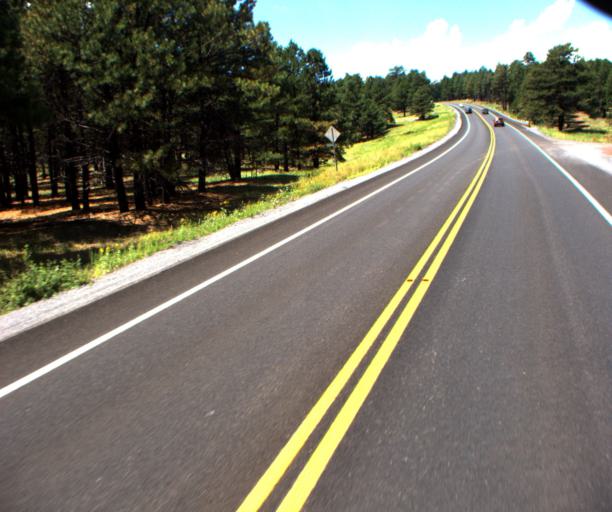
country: US
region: Arizona
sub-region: Coconino County
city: Flagstaff
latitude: 35.1927
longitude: -111.7086
